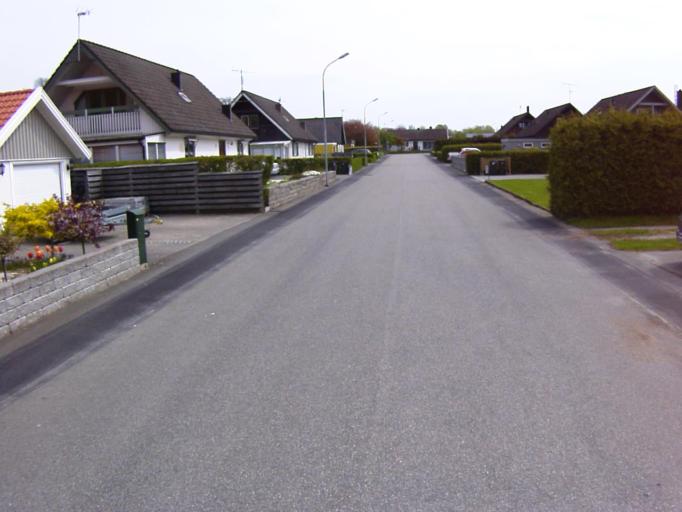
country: SE
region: Skane
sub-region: Kristianstads Kommun
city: Onnestad
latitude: 55.9377
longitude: 13.9841
